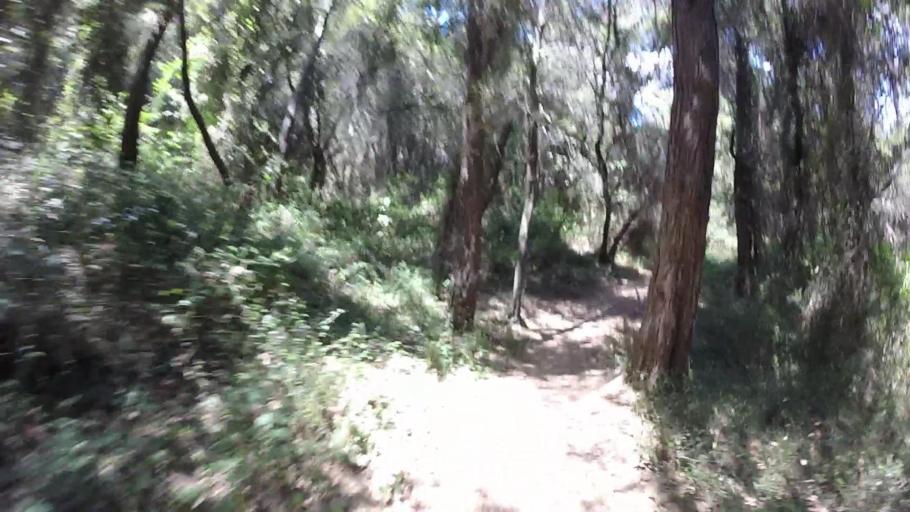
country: FR
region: Provence-Alpes-Cote d'Azur
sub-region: Departement des Alpes-Maritimes
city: Mougins
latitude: 43.5993
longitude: 7.0239
